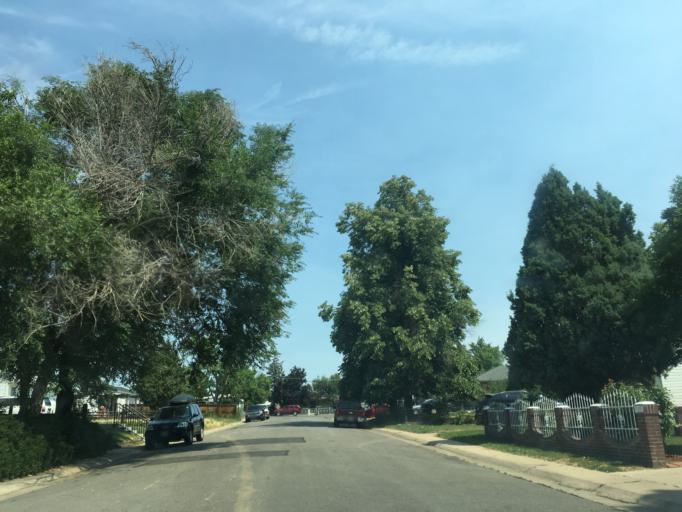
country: US
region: Colorado
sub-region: Jefferson County
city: Lakewood
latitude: 39.6958
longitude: -105.0472
